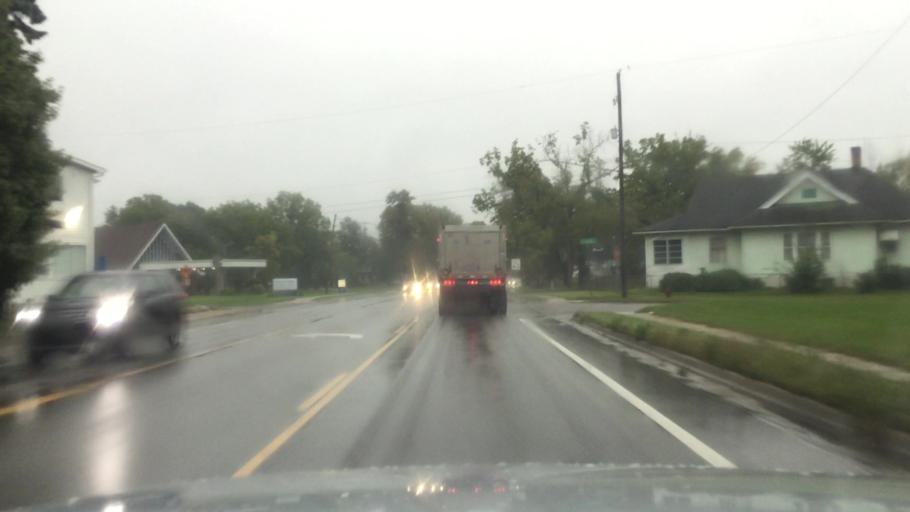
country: US
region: Michigan
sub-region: Saginaw County
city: Saginaw
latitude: 43.3982
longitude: -83.9574
